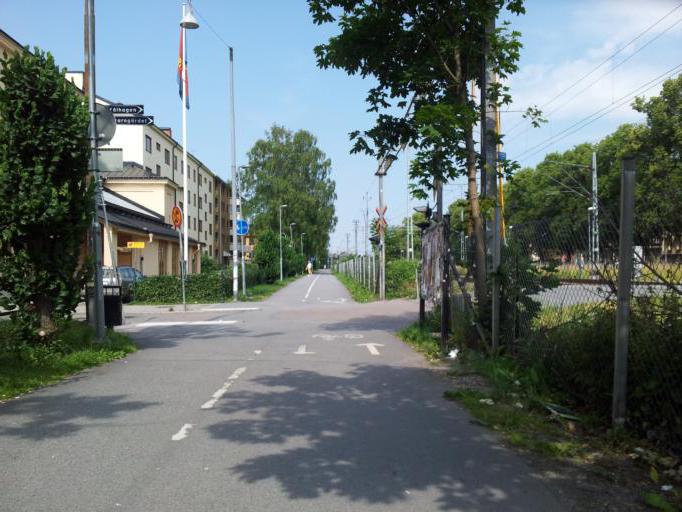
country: SE
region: Uppsala
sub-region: Uppsala Kommun
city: Uppsala
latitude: 59.8611
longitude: 17.6416
